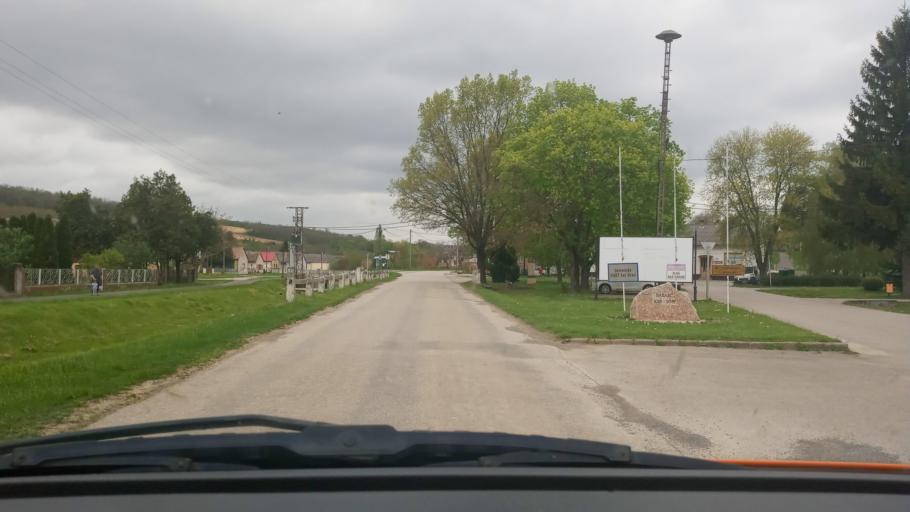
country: HU
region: Baranya
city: Boly
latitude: 46.0052
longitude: 18.5506
